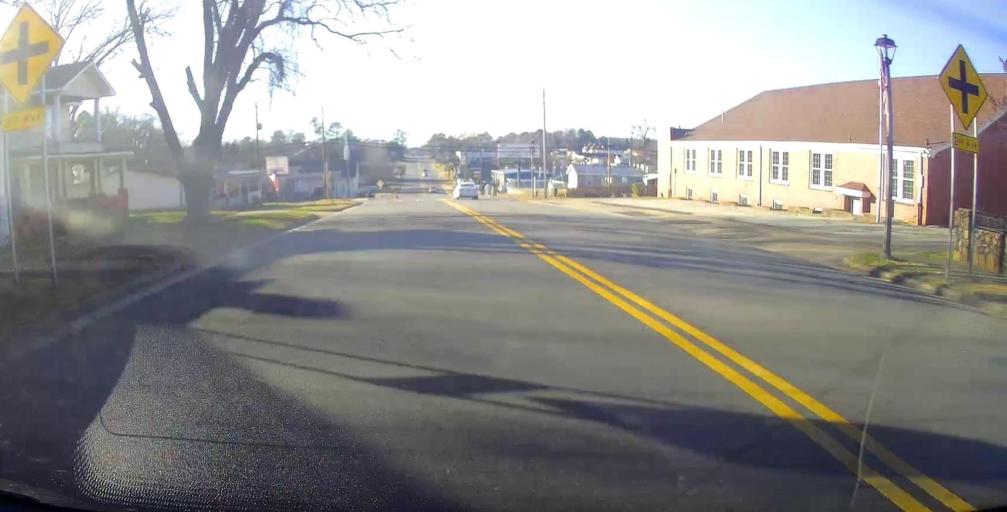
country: US
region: Georgia
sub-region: Meriwether County
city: Manchester
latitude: 32.8516
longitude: -84.6149
